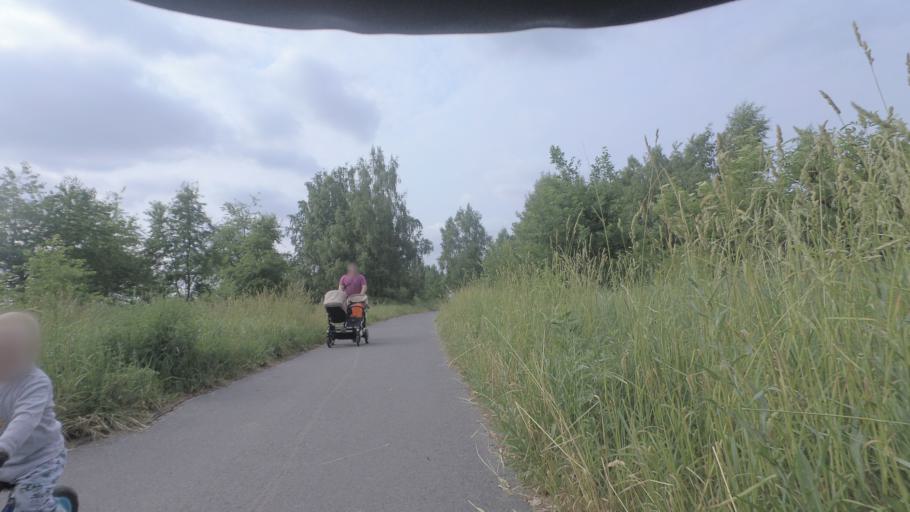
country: DE
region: Berlin
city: Gropiusstadt
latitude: 52.4151
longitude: 13.4694
